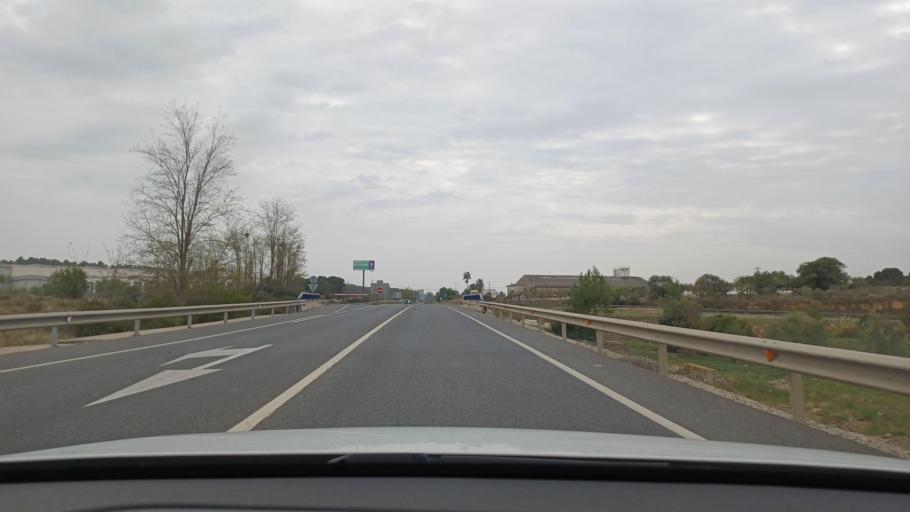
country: ES
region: Catalonia
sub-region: Provincia de Tarragona
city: la Pobla de Mafumet
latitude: 41.1878
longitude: 1.2423
